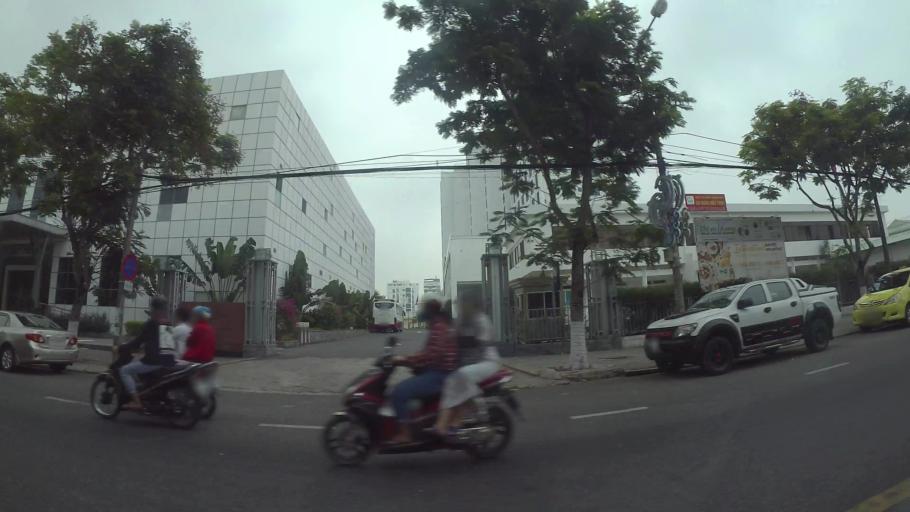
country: VN
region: Da Nang
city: Son Tra
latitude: 16.0554
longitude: 108.2433
